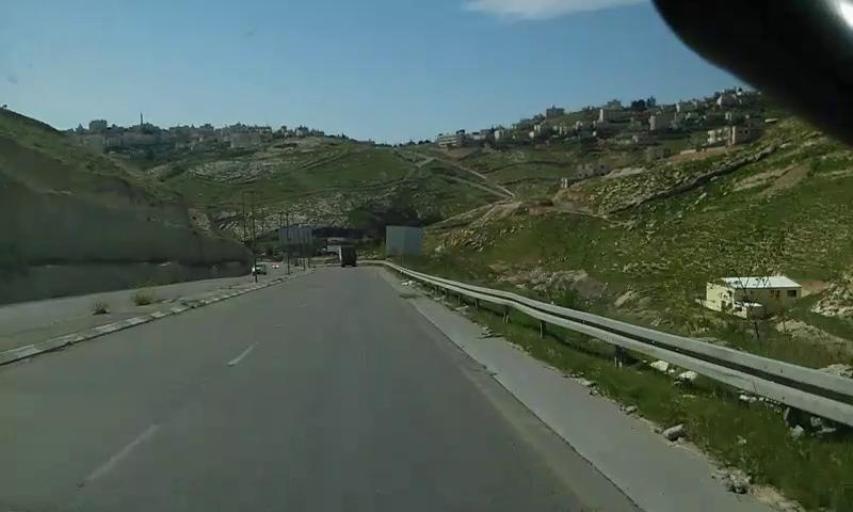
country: PS
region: West Bank
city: Abu Dis
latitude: 31.7479
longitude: 35.2792
